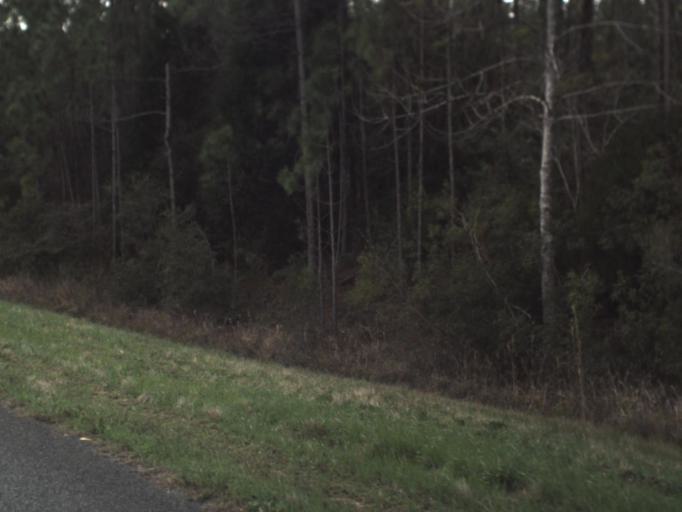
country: US
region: Florida
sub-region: Washington County
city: Chipley
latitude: 30.5961
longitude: -85.3964
